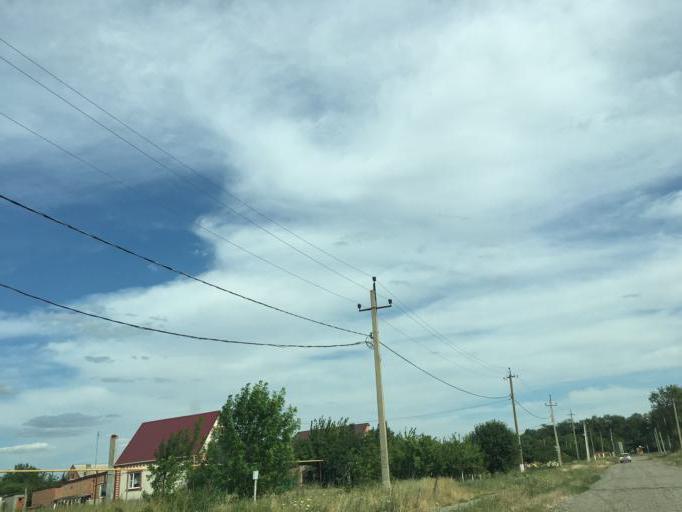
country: RU
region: Krasnodarskiy
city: Kushchevskaya
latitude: 46.5500
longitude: 39.6710
